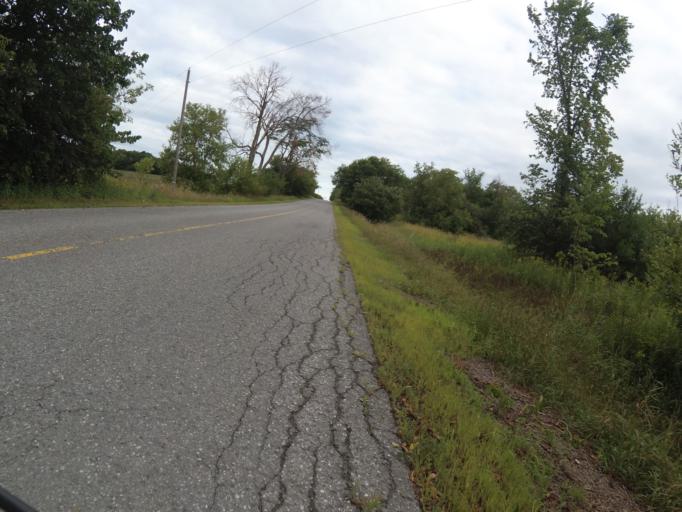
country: CA
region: Ontario
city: Clarence-Rockland
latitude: 45.4286
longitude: -75.2990
